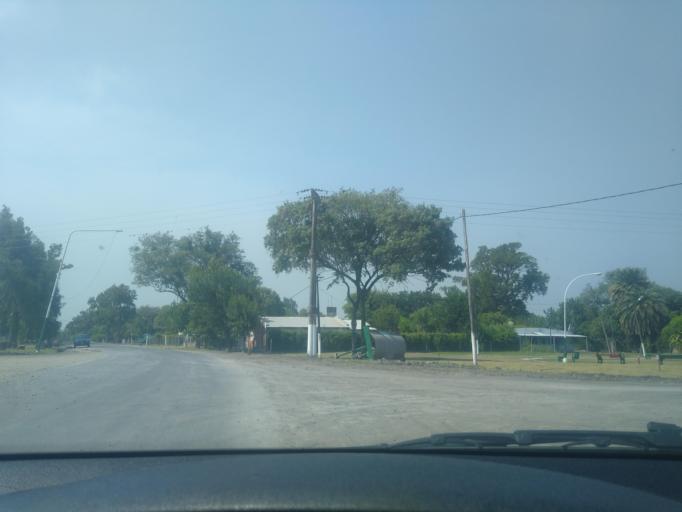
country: AR
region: Chaco
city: Puerto Tirol
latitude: -27.5630
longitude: -59.3062
